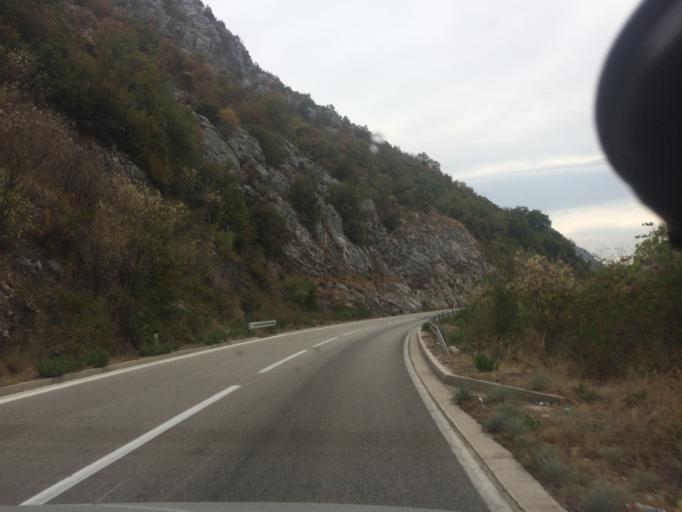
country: ME
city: Lipci
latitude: 42.4934
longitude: 18.6463
